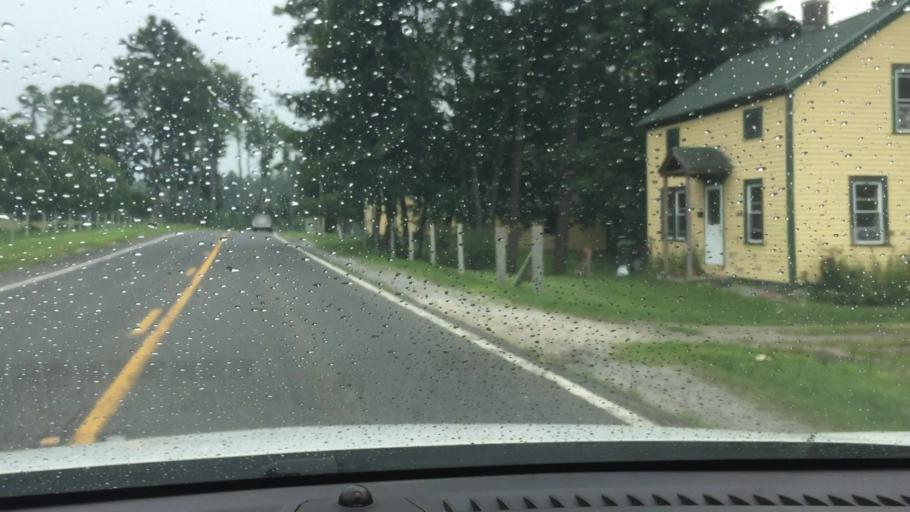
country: US
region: Massachusetts
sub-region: Berkshire County
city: Lee
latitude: 42.3150
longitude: -73.2862
